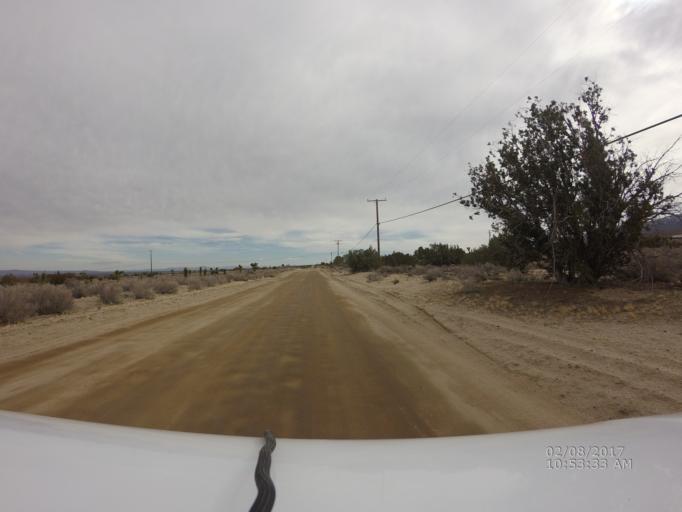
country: US
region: California
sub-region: San Bernardino County
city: Pinon Hills
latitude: 34.4695
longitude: -117.7317
